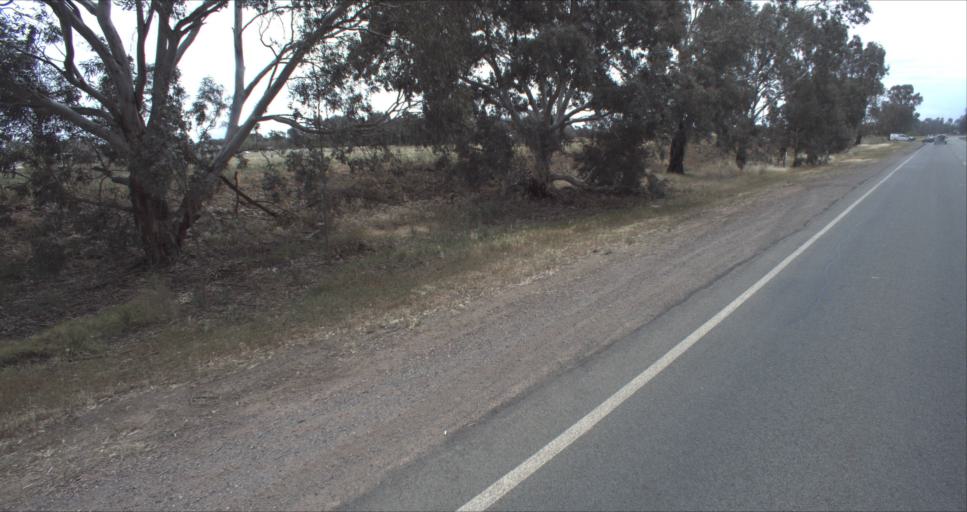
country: AU
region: New South Wales
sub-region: Leeton
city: Leeton
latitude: -34.5312
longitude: 146.4095
